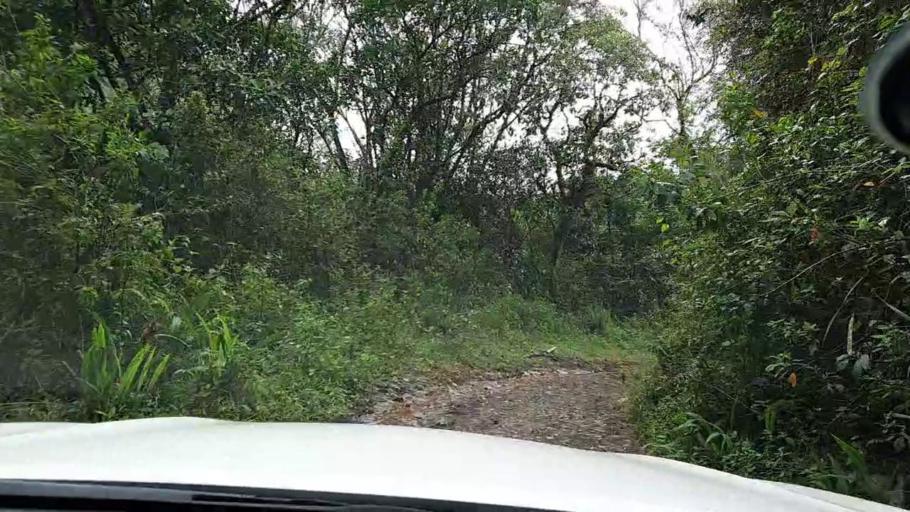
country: RW
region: Western Province
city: Kibuye
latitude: -2.2800
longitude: 29.3055
